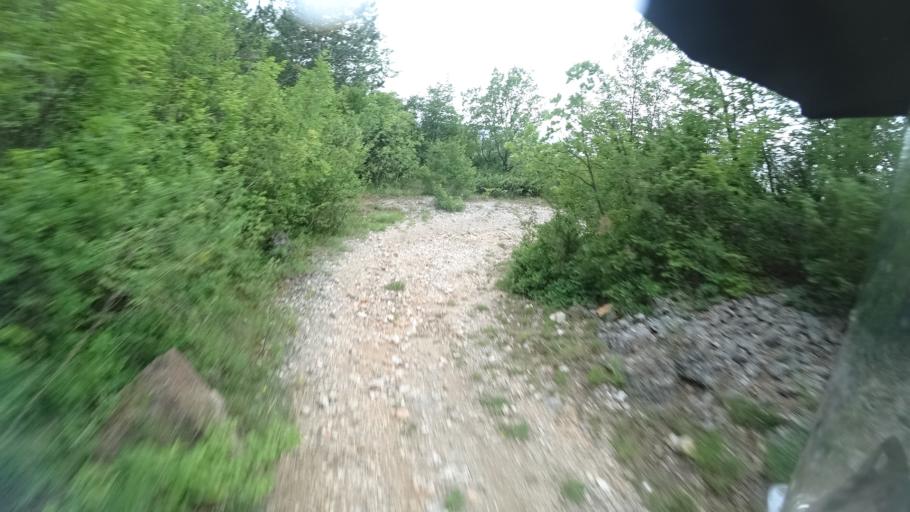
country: HR
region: Sibensko-Kniniska
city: Knin
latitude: 44.0331
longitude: 16.2282
